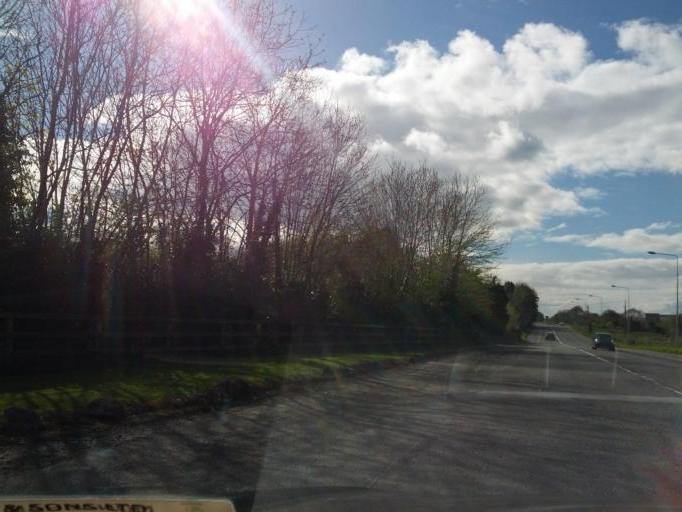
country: IE
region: Leinster
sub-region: Kildare
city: Kilcock
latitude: 53.4056
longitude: -6.6809
